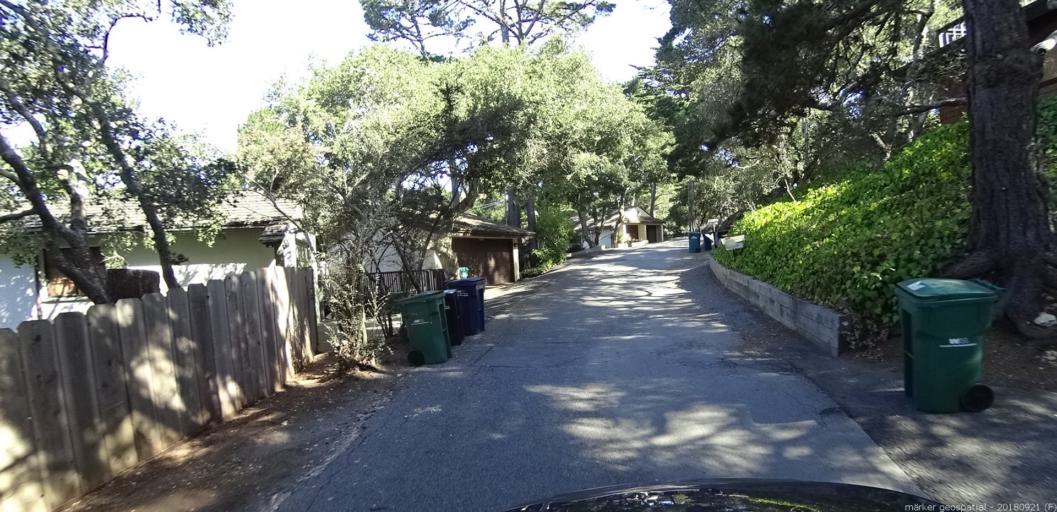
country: US
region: California
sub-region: Monterey County
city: Carmel-by-the-Sea
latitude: 36.5648
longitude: -121.9147
